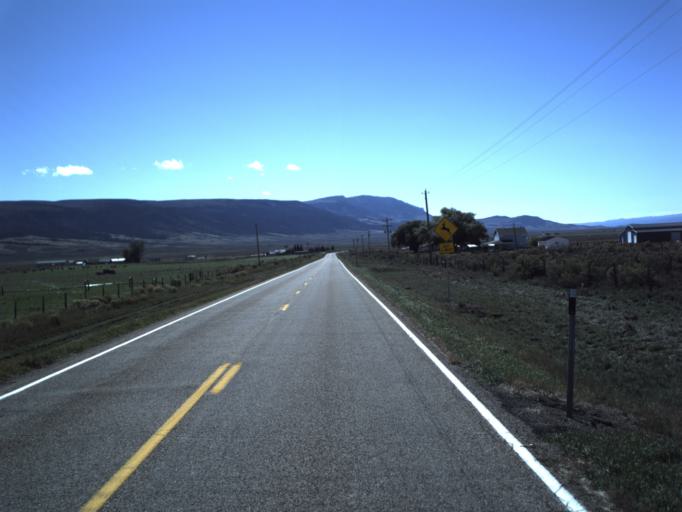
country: US
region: Utah
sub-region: Wayne County
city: Loa
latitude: 38.5041
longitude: -111.8814
